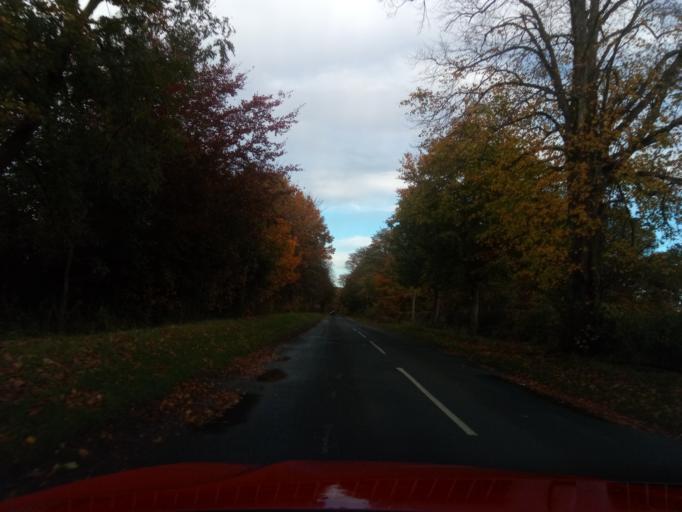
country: GB
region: England
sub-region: Northumberland
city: Ford
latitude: 55.6295
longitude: -2.1031
